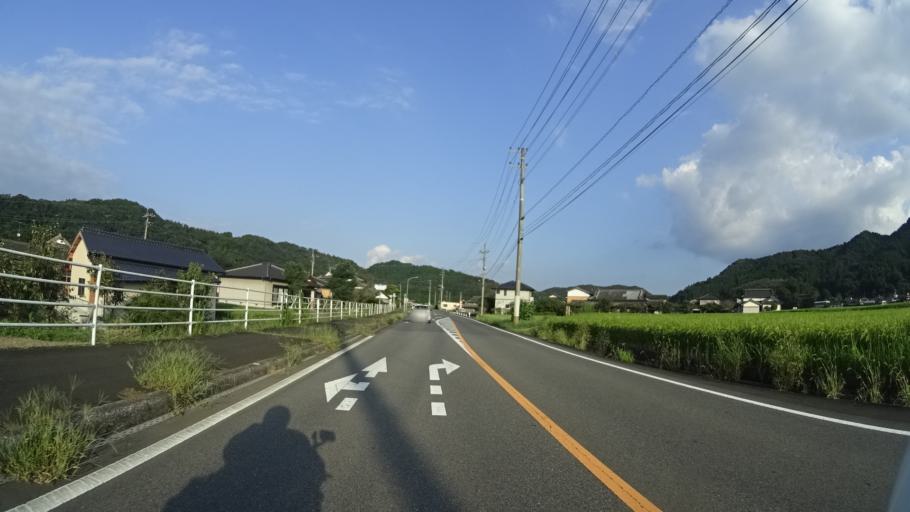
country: JP
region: Oita
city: Bungo-Takada-shi
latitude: 33.4351
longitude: 131.3654
